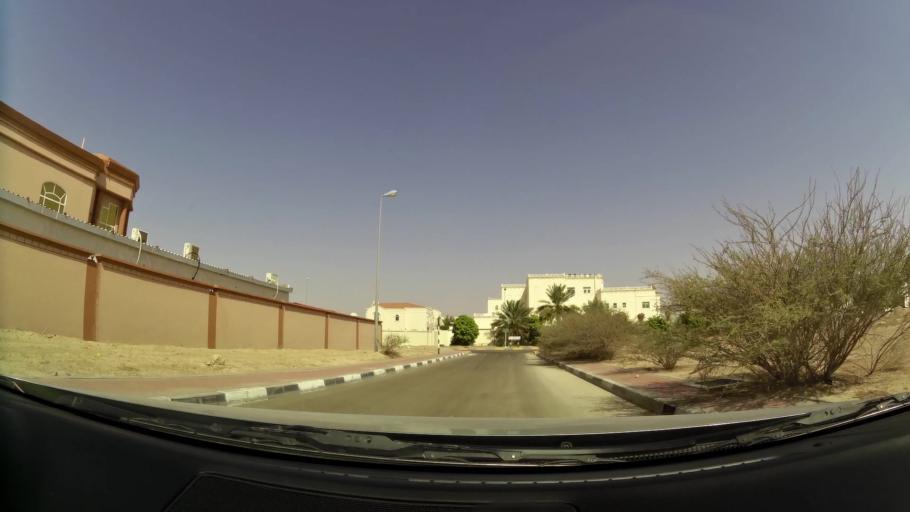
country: OM
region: Al Buraimi
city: Al Buraymi
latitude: 24.3172
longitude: 55.8066
